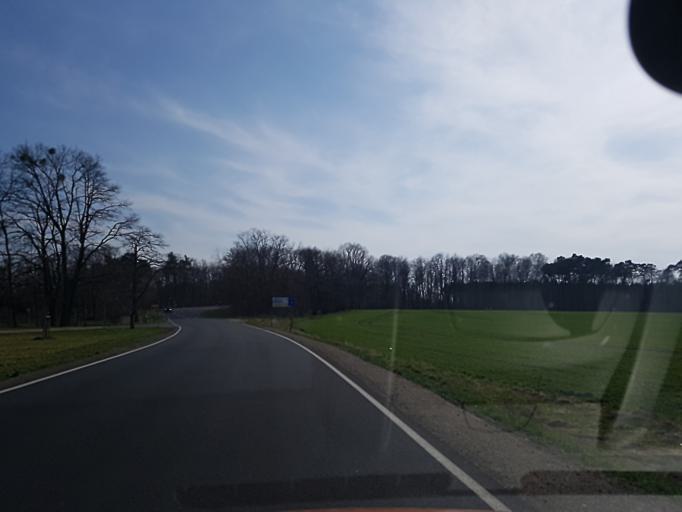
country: DE
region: Brandenburg
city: Bronkow
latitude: 51.6677
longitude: 13.9119
